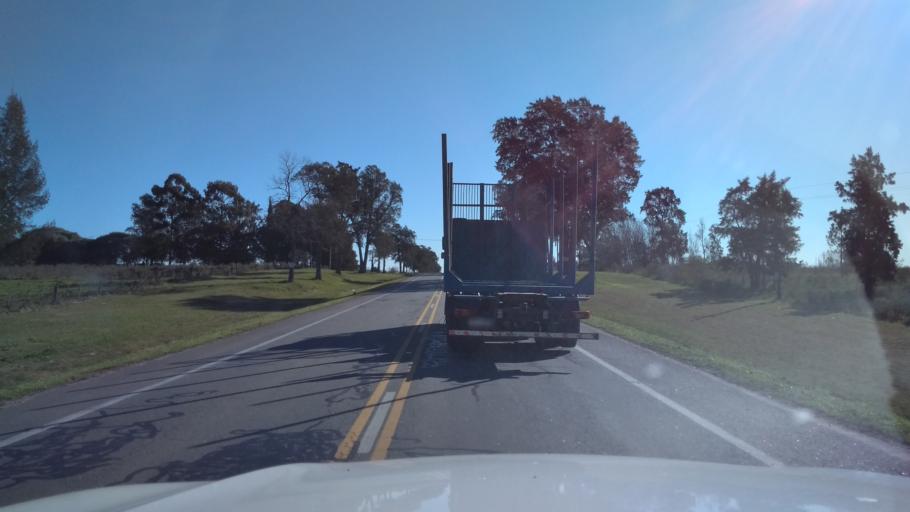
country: UY
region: Canelones
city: San Jacinto
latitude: -34.5408
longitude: -55.8923
